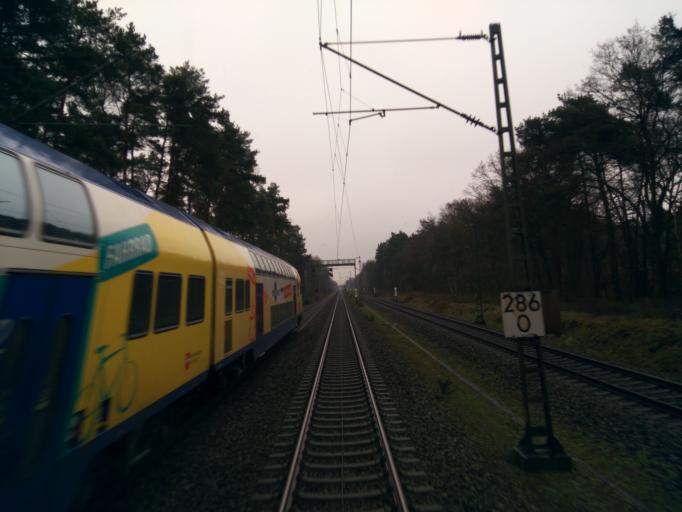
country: DE
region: Lower Saxony
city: Rotenburg
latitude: 53.1290
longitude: 9.4351
